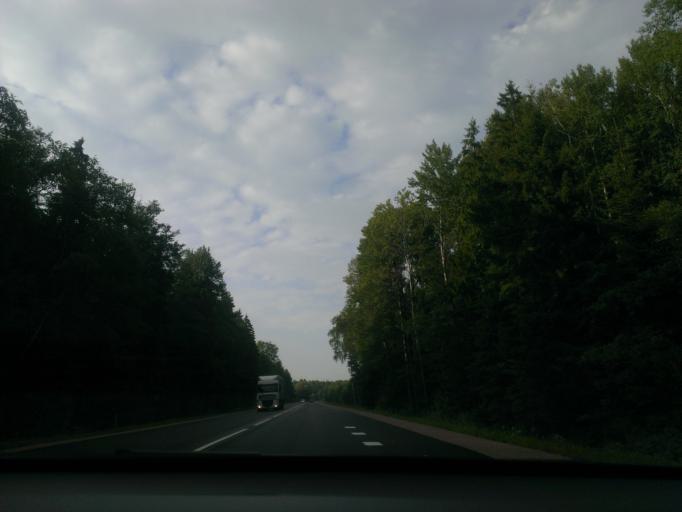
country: LV
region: Kekava
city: Kekava
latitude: 56.7114
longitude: 24.2473
